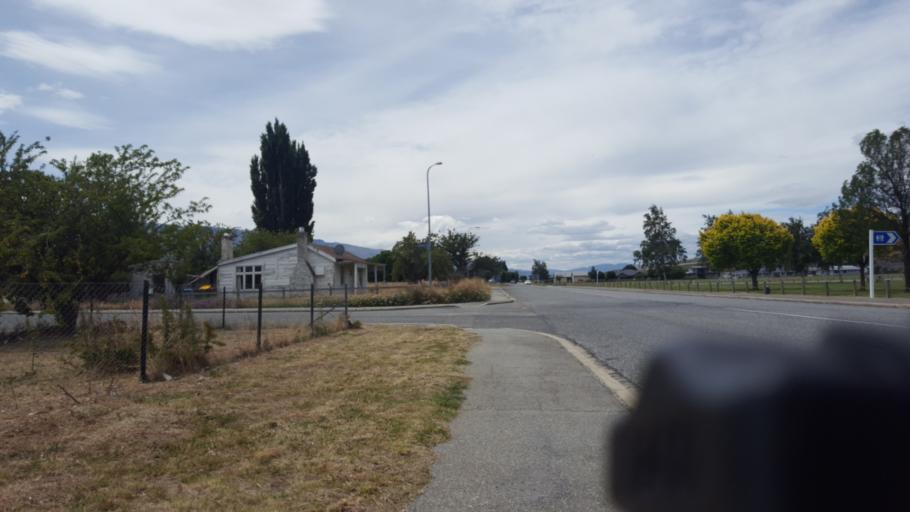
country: NZ
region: Otago
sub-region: Queenstown-Lakes District
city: Wanaka
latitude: -45.0434
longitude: 169.2135
